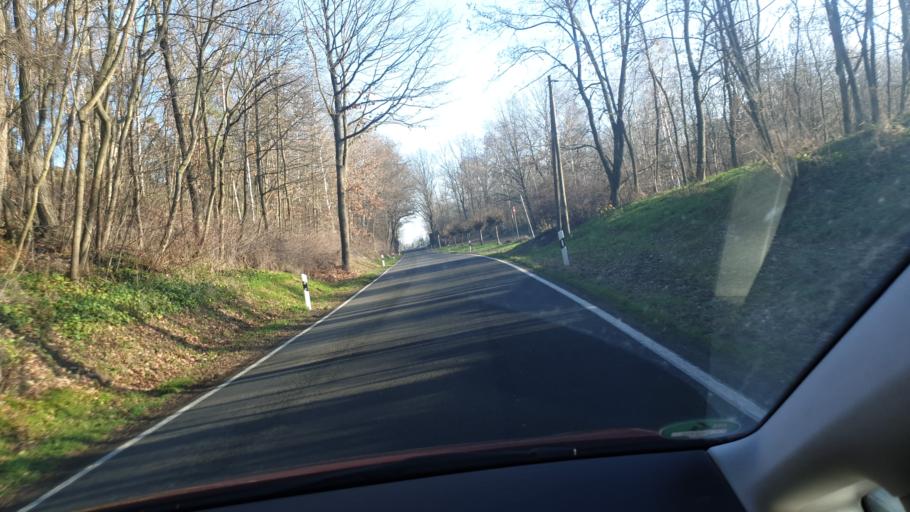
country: DE
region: Saxony
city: Hohburg
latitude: 51.4110
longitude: 12.7884
